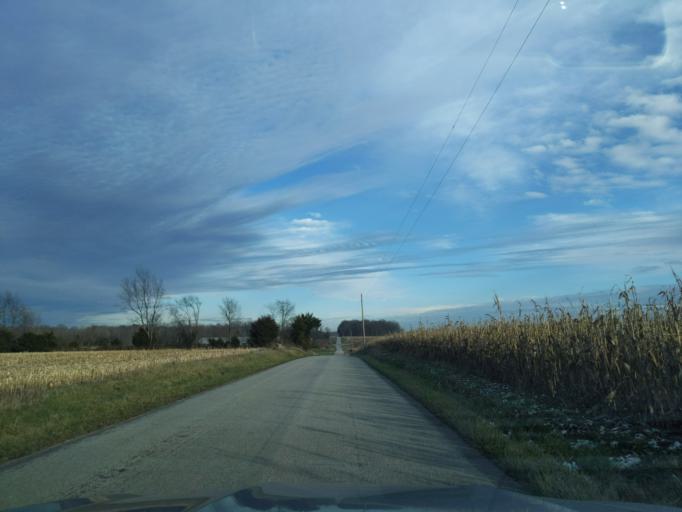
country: US
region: Indiana
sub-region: Decatur County
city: Westport
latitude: 39.2192
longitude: -85.4851
